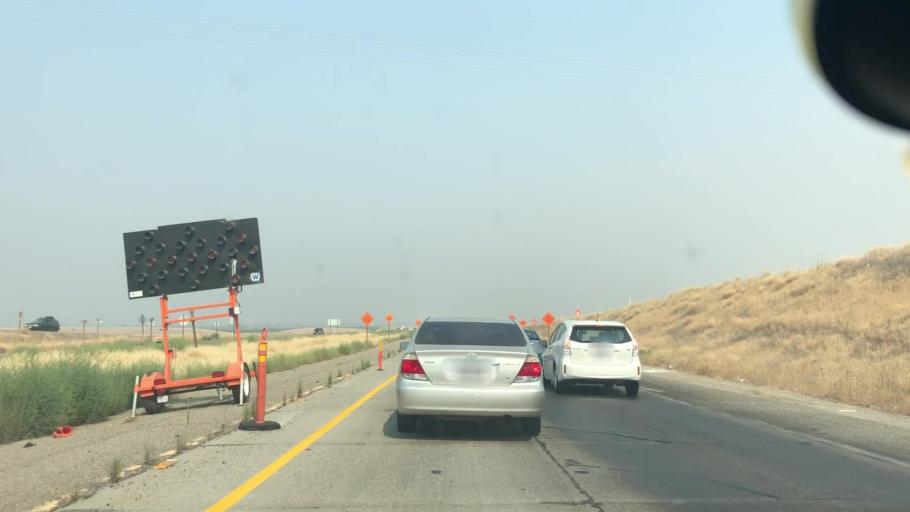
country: US
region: California
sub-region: San Joaquin County
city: Tracy
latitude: 37.6385
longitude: -121.3975
